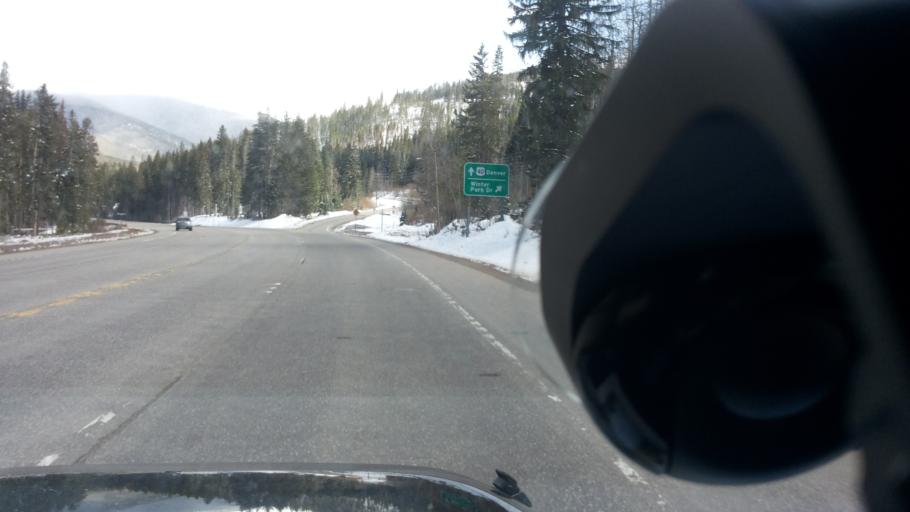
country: US
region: Colorado
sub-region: Grand County
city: Fraser
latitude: 39.9016
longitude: -105.7790
